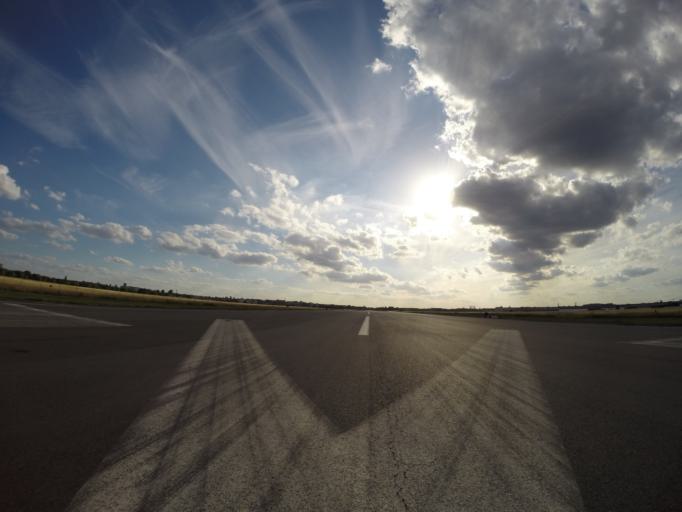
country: DE
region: Berlin
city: Tempelhof Bezirk
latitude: 52.4713
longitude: 13.4115
